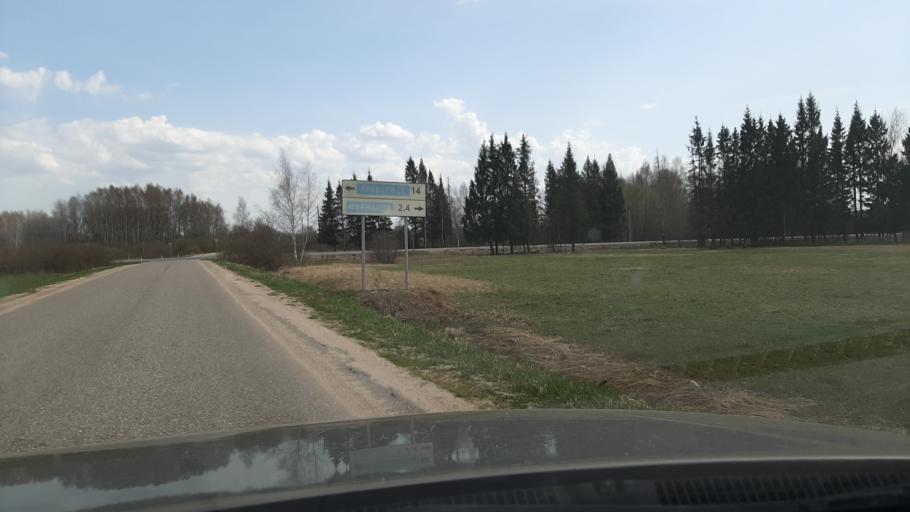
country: RU
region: Ivanovo
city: Furmanov
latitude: 57.2943
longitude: 41.1772
